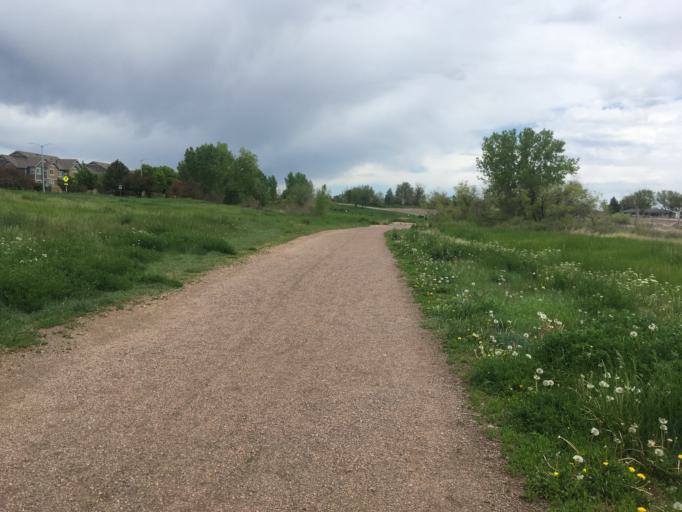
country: US
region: Colorado
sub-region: Adams County
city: Northglenn
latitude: 39.9537
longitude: -105.0167
